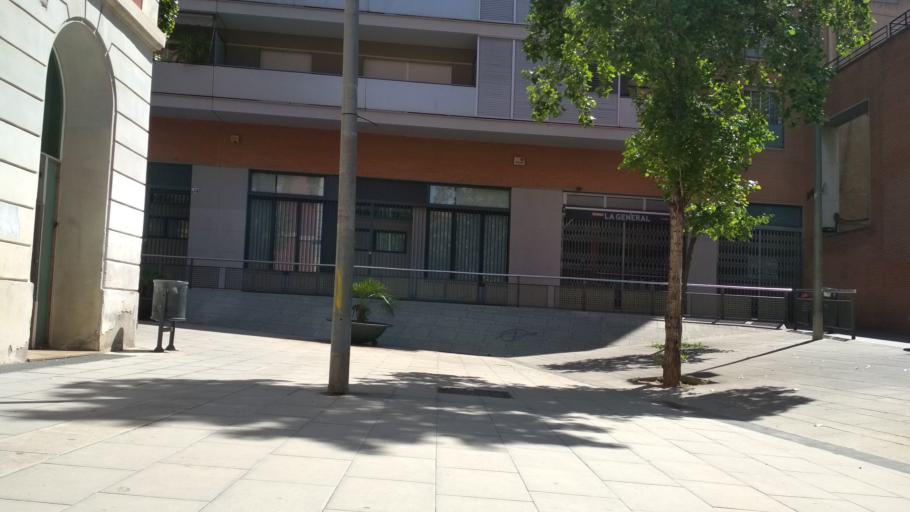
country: ES
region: Catalonia
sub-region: Provincia de Barcelona
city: les Corts
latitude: 41.3768
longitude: 2.1348
